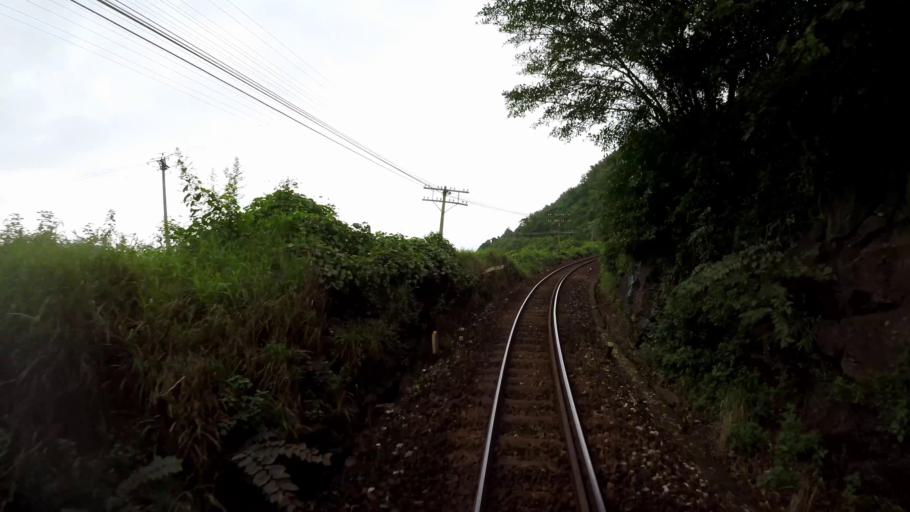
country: VN
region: Da Nang
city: Lien Chieu
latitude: 16.2104
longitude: 108.1227
